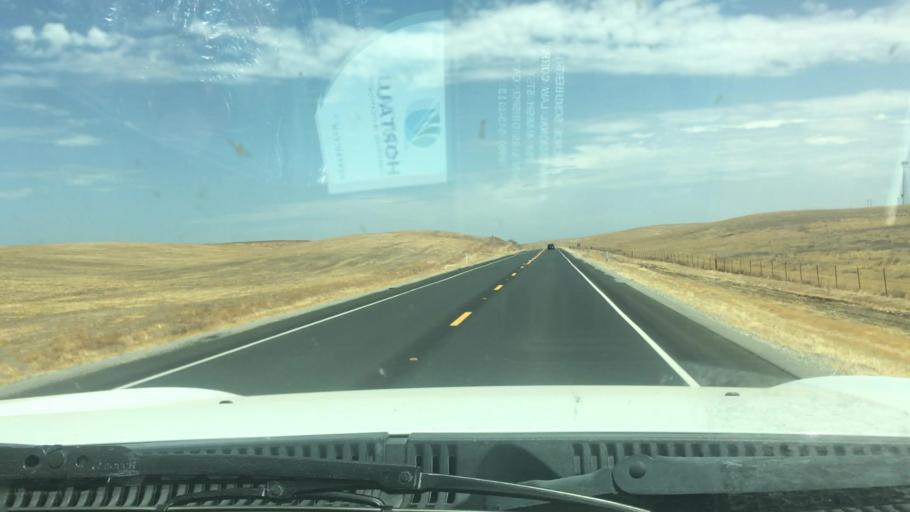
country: US
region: California
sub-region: Kern County
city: McFarland
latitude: 35.6202
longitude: -119.0858
